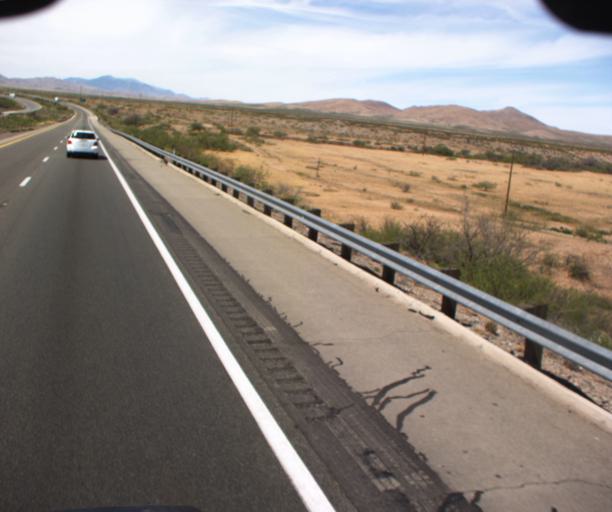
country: US
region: Arizona
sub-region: Cochise County
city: Willcox
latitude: 32.3546
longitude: -109.6100
